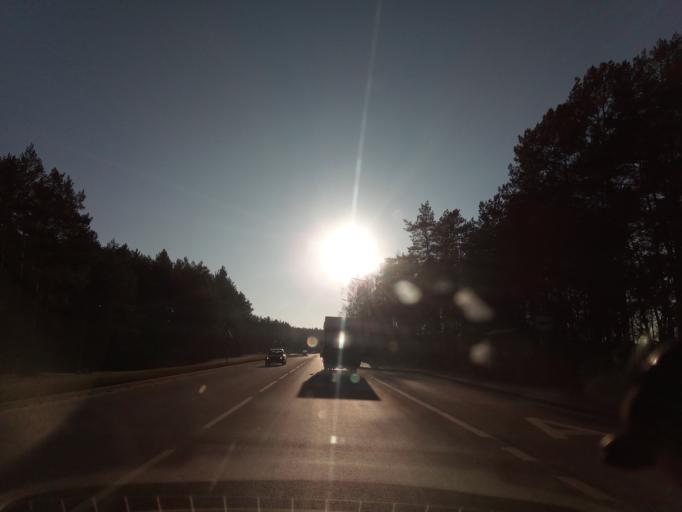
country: LT
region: Alytaus apskritis
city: Druskininkai
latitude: 54.0132
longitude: 23.9947
